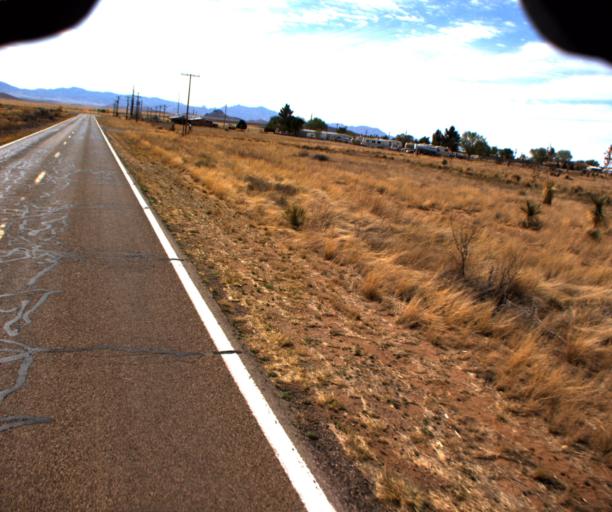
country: US
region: Arizona
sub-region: Cochise County
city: Willcox
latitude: 31.8837
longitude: -109.6908
